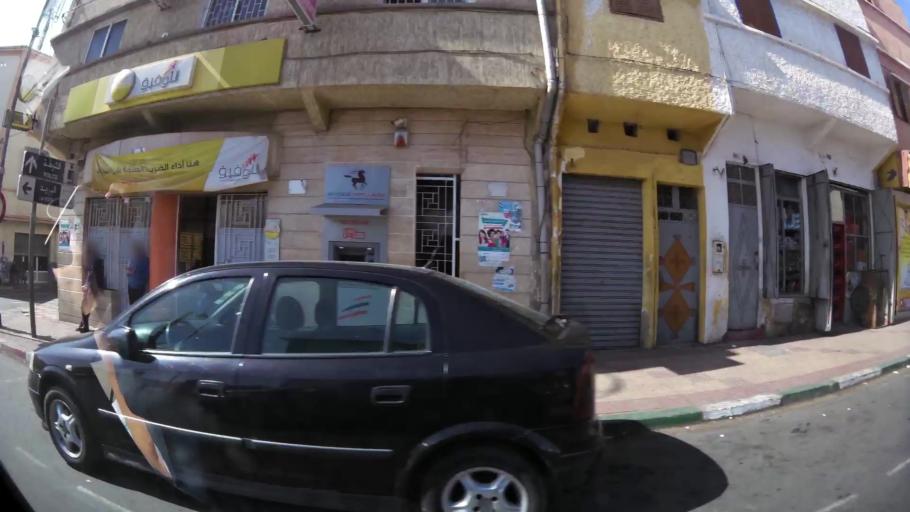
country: MA
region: Souss-Massa-Draa
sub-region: Inezgane-Ait Mellou
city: Inezgane
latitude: 30.3703
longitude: -9.5388
